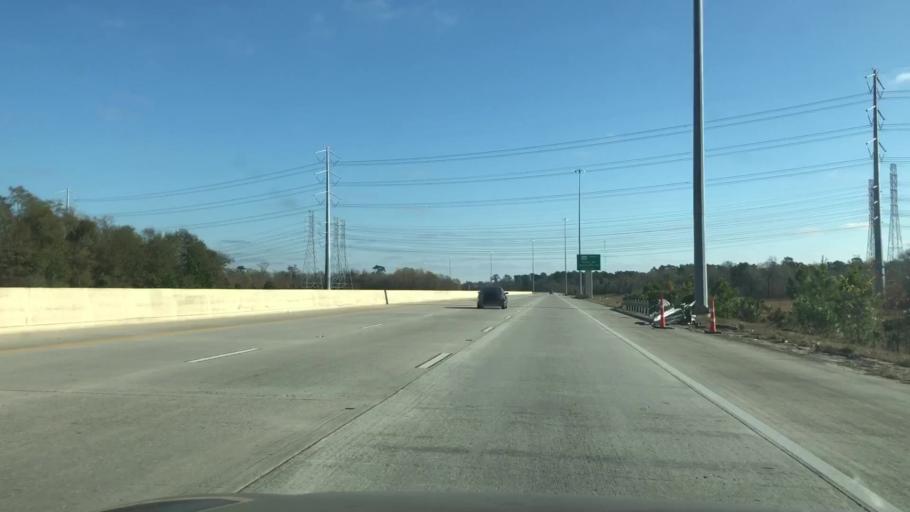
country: US
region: Texas
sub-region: Harris County
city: Jacinto City
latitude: 29.7920
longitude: -95.2342
